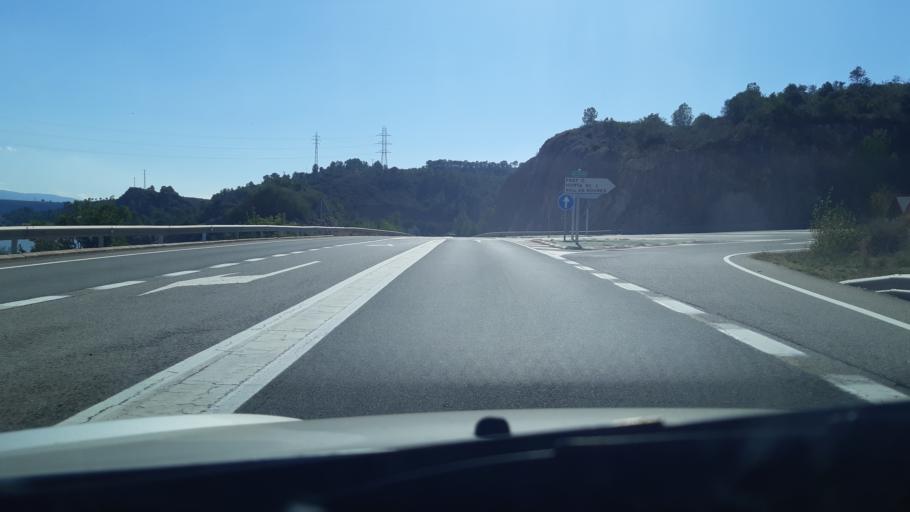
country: ES
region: Catalonia
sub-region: Provincia de Tarragona
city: Tivenys
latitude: 40.9328
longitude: 0.4849
